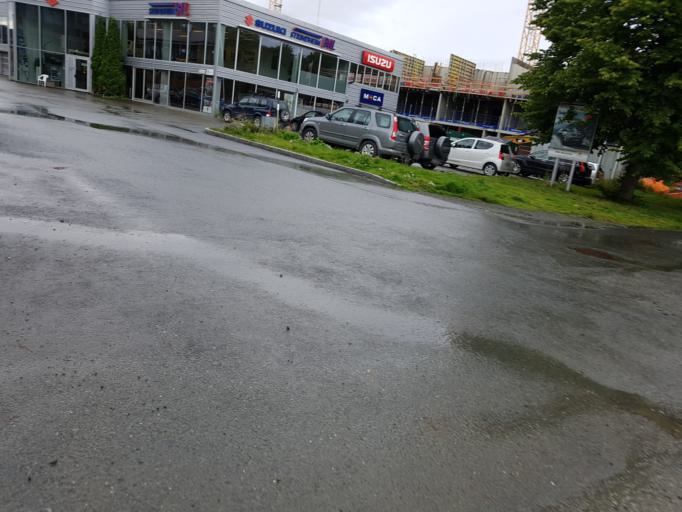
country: NO
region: Sor-Trondelag
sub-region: Trondheim
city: Trondheim
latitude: 63.4430
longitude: 10.4614
